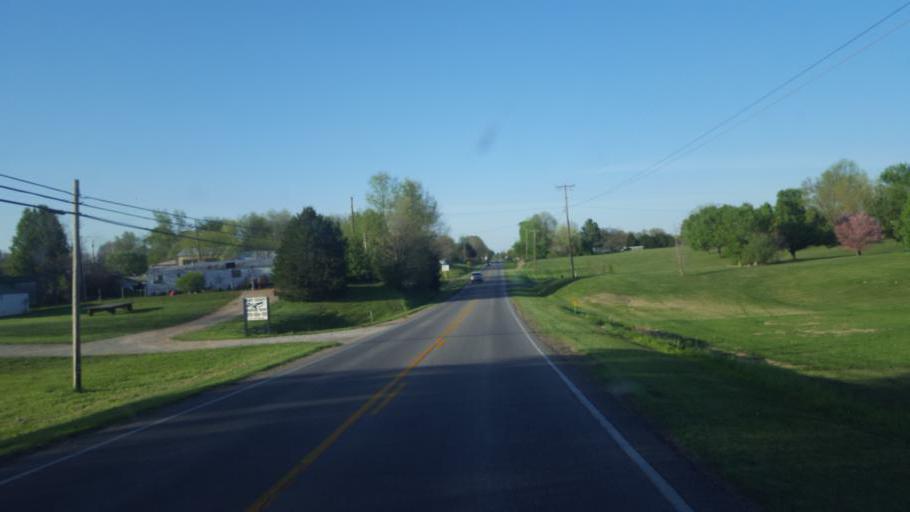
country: US
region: Kentucky
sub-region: Hart County
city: Munfordville
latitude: 37.2537
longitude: -85.8875
